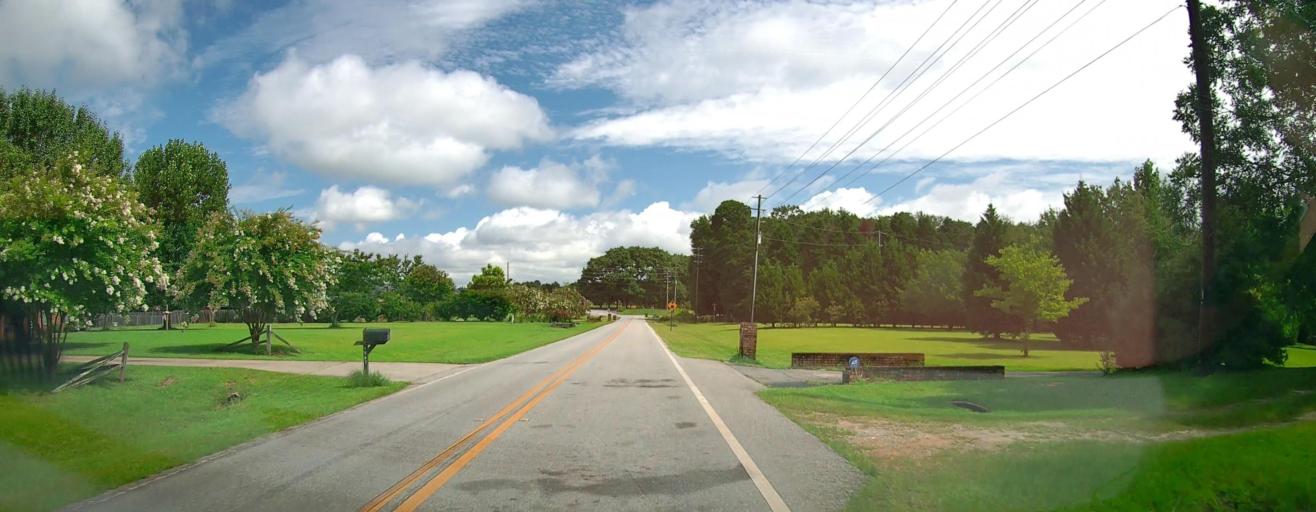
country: US
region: Georgia
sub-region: Peach County
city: Byron
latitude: 32.6352
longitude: -83.8000
